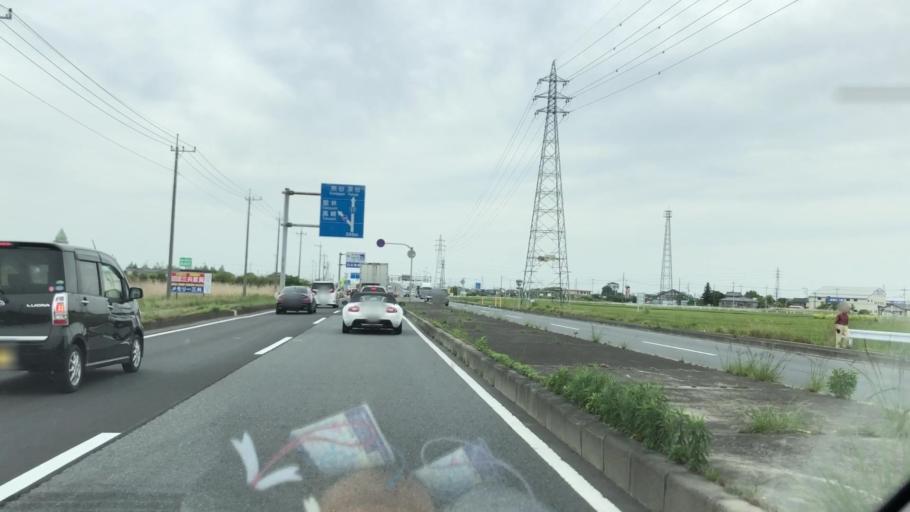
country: JP
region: Gunma
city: Sakai-nakajima
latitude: 36.2658
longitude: 139.2934
